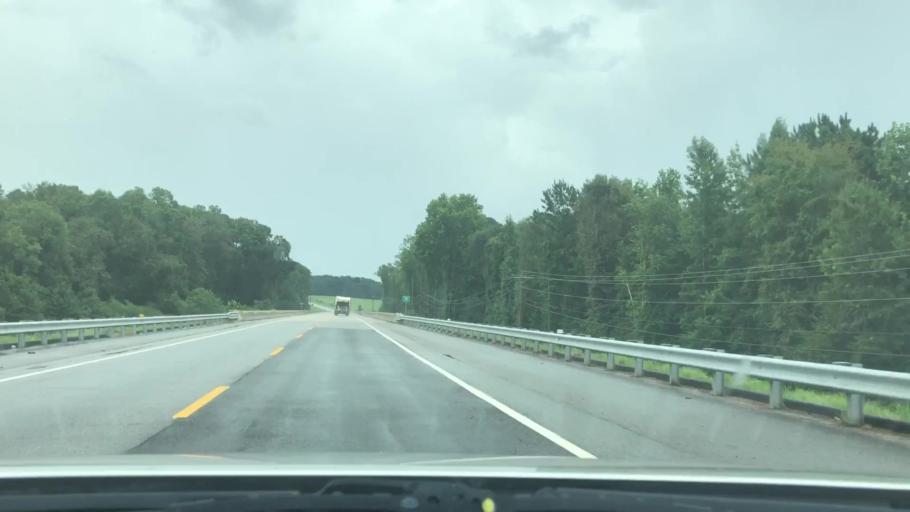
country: US
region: Georgia
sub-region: Lamar County
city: Barnesville
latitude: 33.0684
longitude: -84.2321
